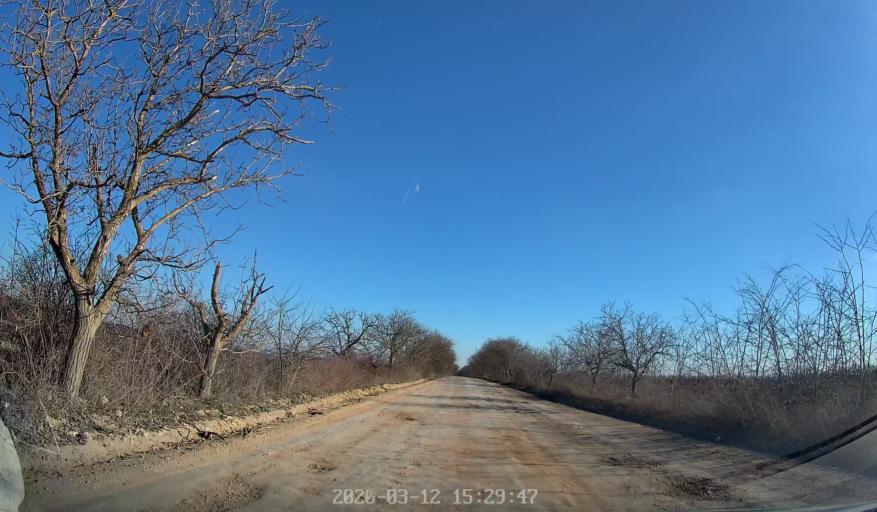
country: MD
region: Chisinau
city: Ciorescu
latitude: 47.1631
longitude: 28.9366
